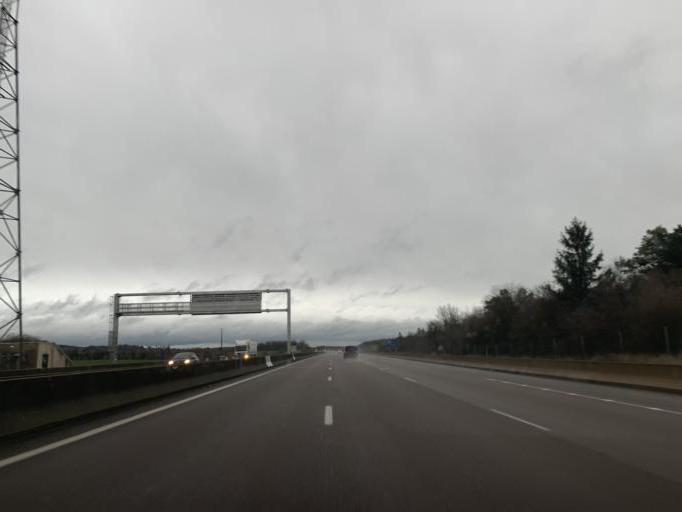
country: FR
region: Champagne-Ardenne
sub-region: Departement de la Haute-Marne
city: Langres
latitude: 47.8214
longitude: 5.2249
